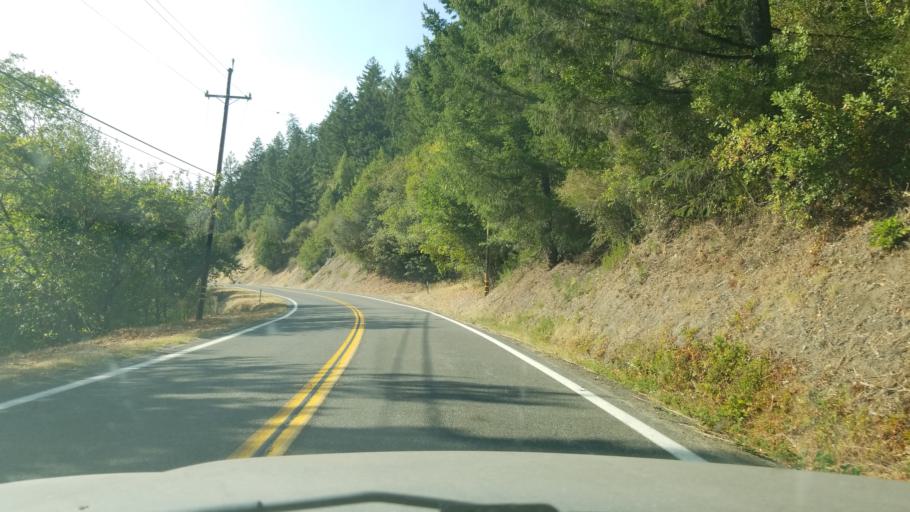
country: US
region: California
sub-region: Humboldt County
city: Redway
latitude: 40.2024
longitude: -123.7777
